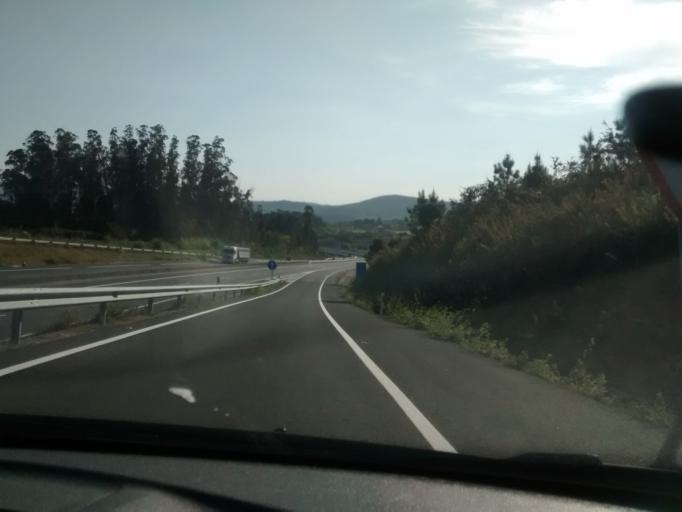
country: ES
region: Galicia
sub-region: Provincia da Coruna
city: Teo
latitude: 42.7983
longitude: -8.5365
